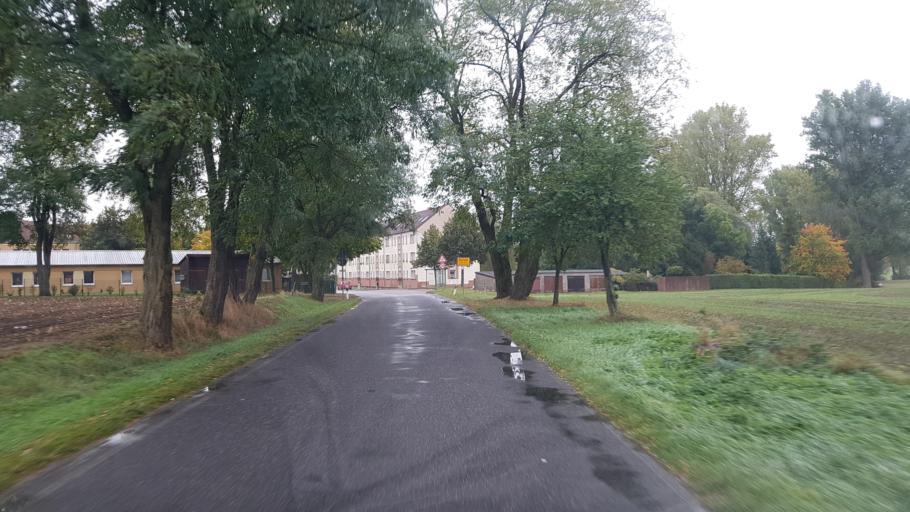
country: DE
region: Brandenburg
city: Furstenwalde
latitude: 52.4291
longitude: 14.0333
